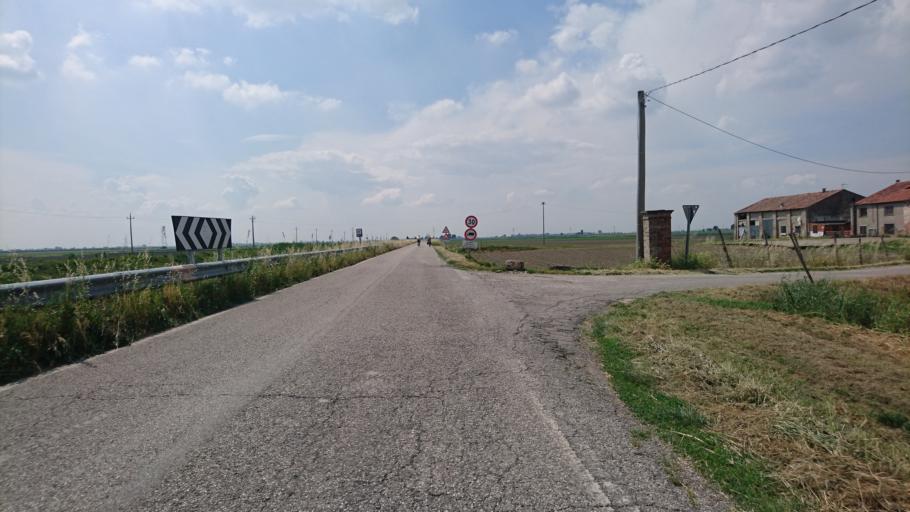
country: IT
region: Veneto
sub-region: Provincia di Rovigo
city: Giacciano con Baruchella
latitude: 45.0711
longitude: 11.4105
